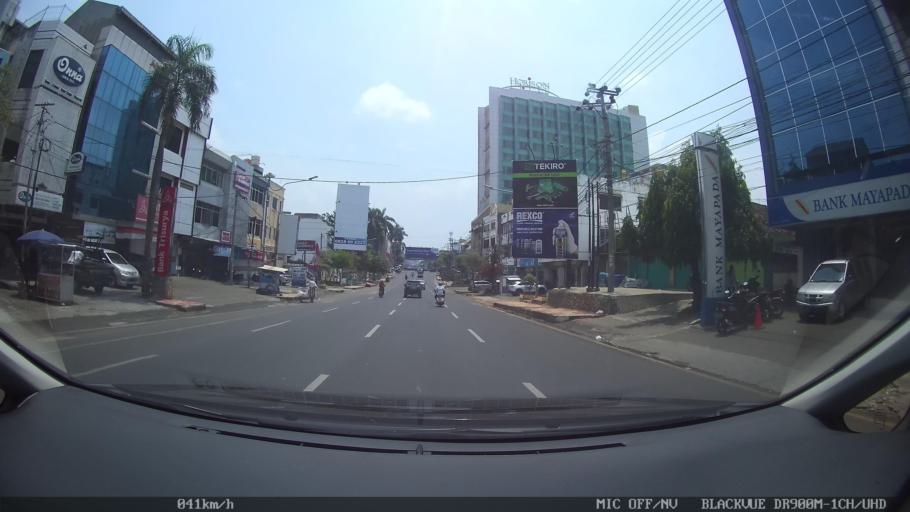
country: ID
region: Lampung
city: Bandarlampung
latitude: -5.4160
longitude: 105.2545
